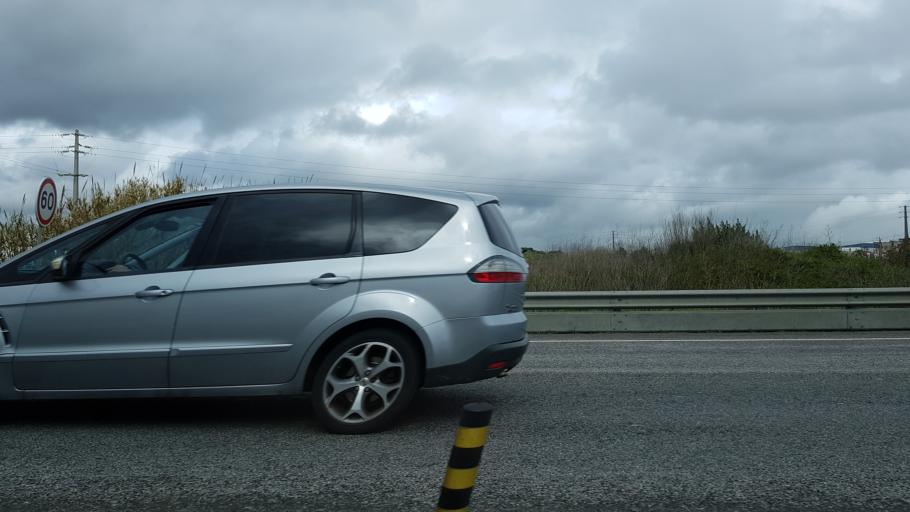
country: PT
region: Lisbon
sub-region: Alenquer
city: Carregado
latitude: 39.0357
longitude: -8.9827
